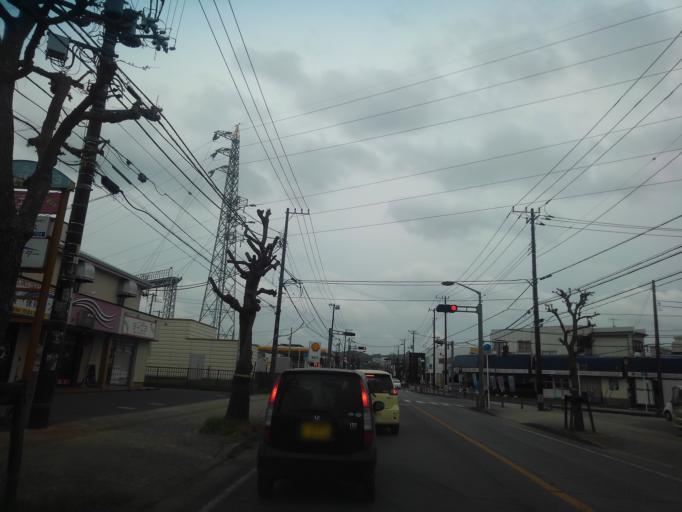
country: JP
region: Chiba
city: Kimitsu
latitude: 35.3222
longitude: 139.9219
